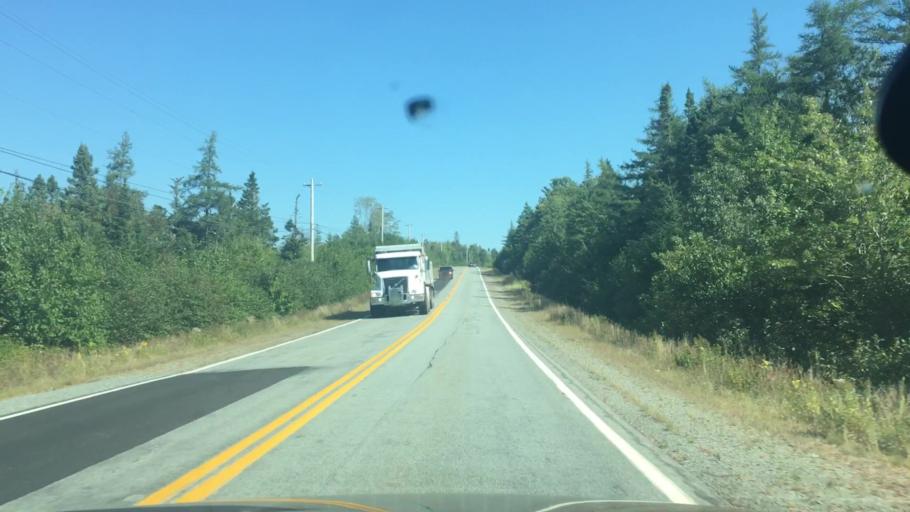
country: CA
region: Nova Scotia
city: New Glasgow
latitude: 44.9057
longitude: -62.5568
